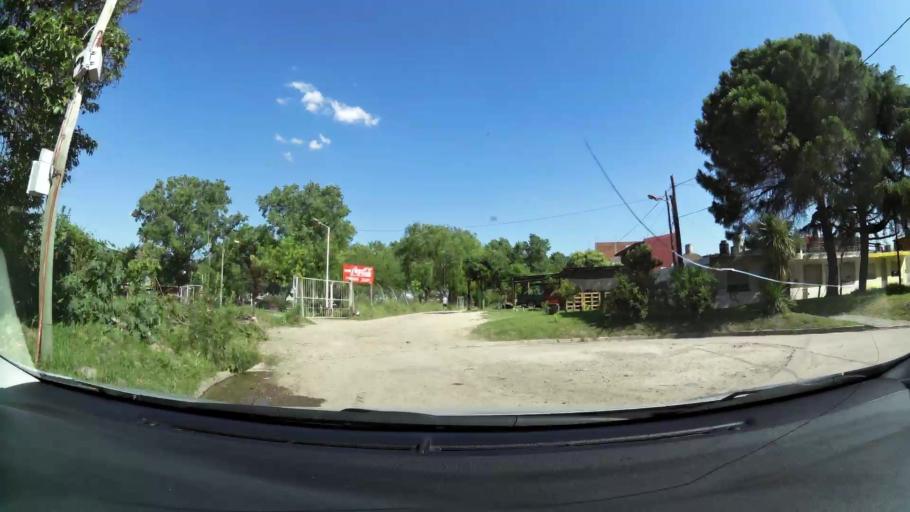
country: AR
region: Buenos Aires F.D.
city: Villa Lugano
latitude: -34.7026
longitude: -58.4701
